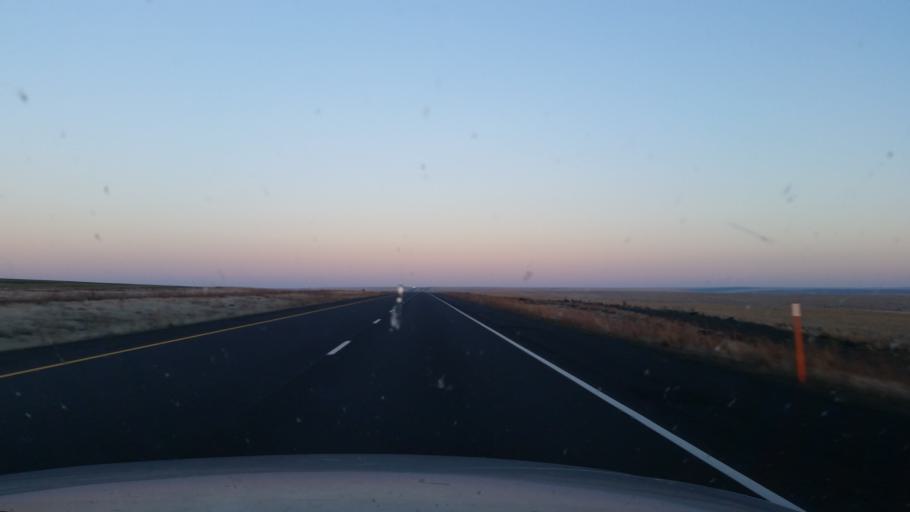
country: US
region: Washington
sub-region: Grant County
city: Warden
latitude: 47.0860
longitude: -118.7806
